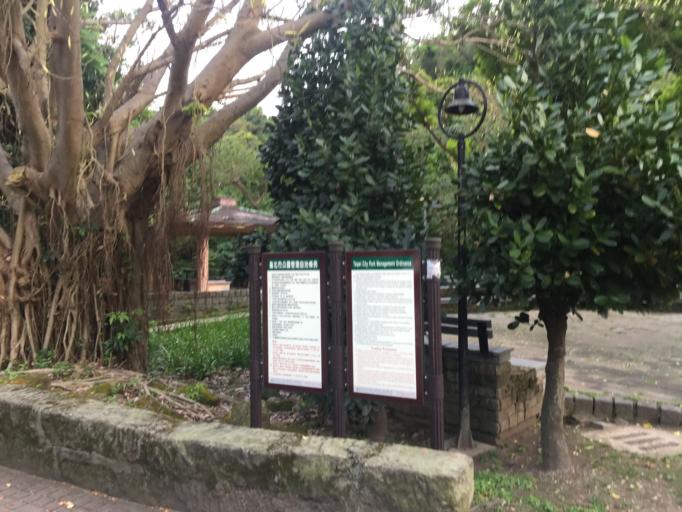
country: TW
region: Taipei
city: Taipei
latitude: 25.1045
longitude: 121.5310
